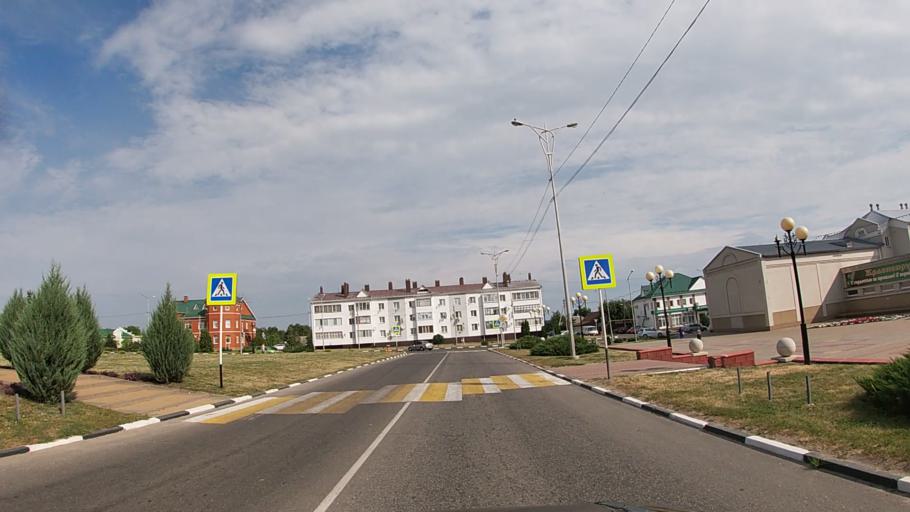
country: RU
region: Belgorod
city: Krasnaya Yaruga
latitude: 50.8020
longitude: 35.6597
